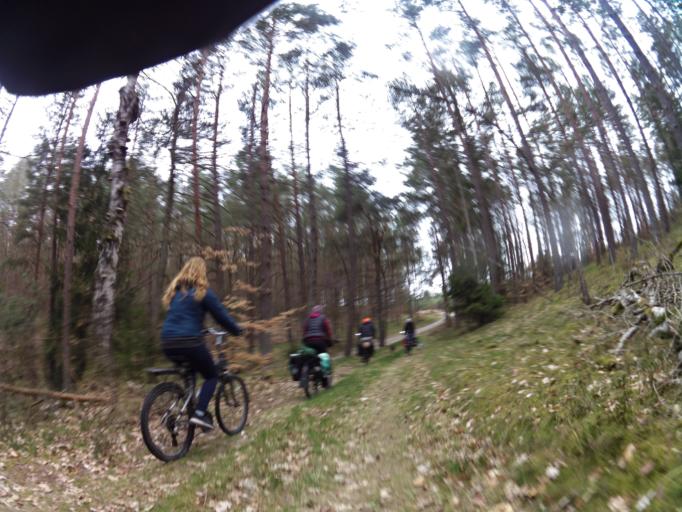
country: PL
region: West Pomeranian Voivodeship
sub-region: Powiat szczecinecki
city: Bialy Bor
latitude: 53.9398
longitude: 16.7319
